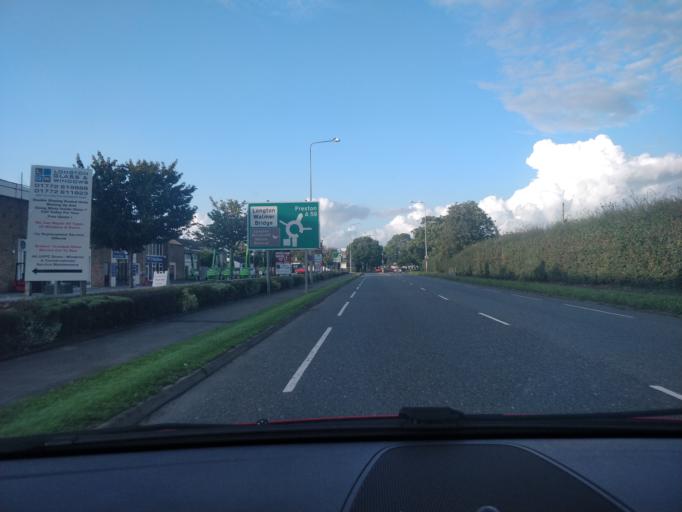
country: GB
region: England
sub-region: Lancashire
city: Tarleton
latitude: 53.7058
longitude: -2.7976
